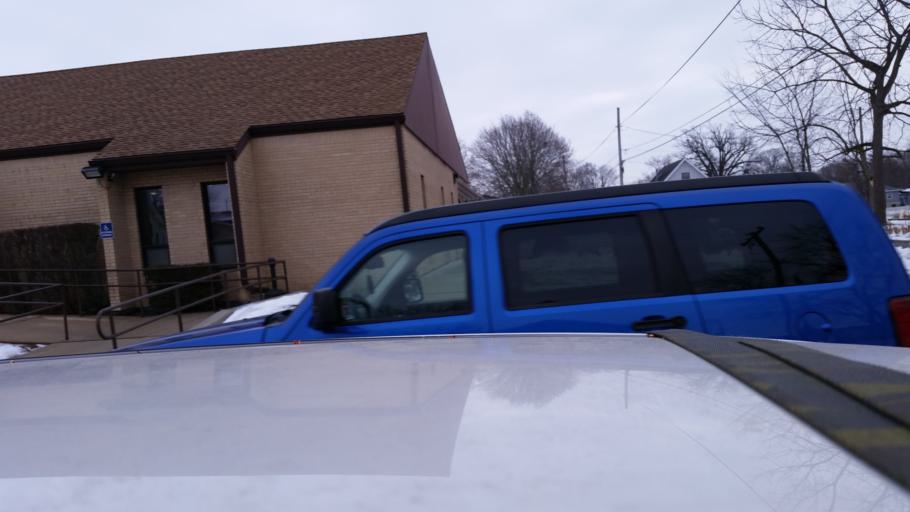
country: US
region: Indiana
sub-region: Howard County
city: Kokomo
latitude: 40.4915
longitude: -86.1256
